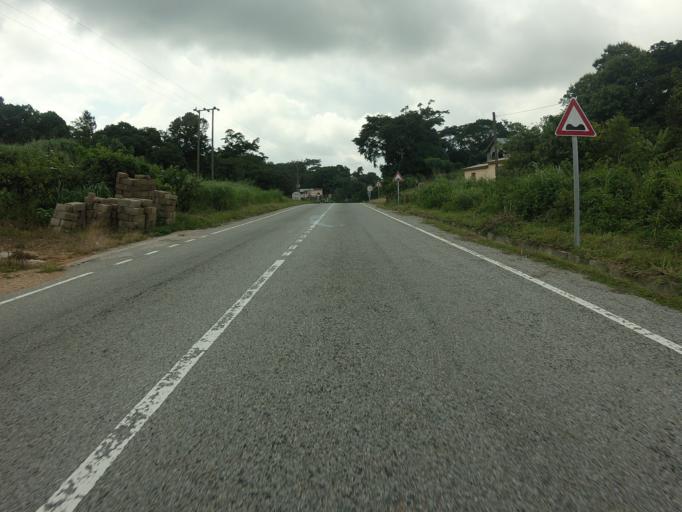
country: GH
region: Volta
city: Kpandu
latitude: 6.8381
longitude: 0.4193
